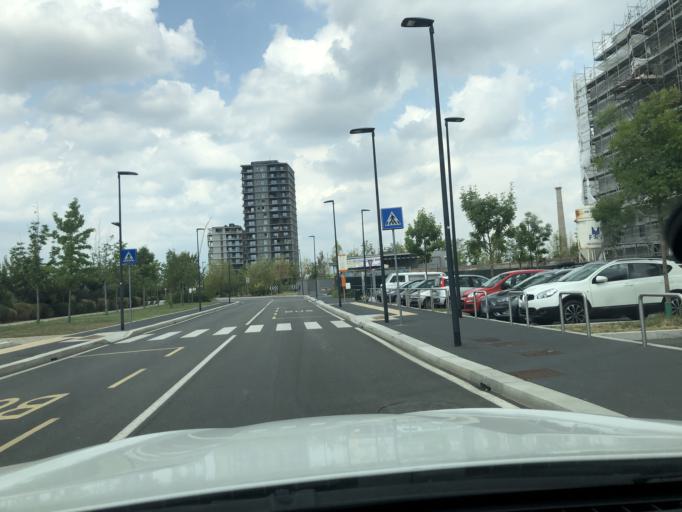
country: IT
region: Lombardy
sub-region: Citta metropolitana di Milano
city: Pero
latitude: 45.5059
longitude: 9.1039
